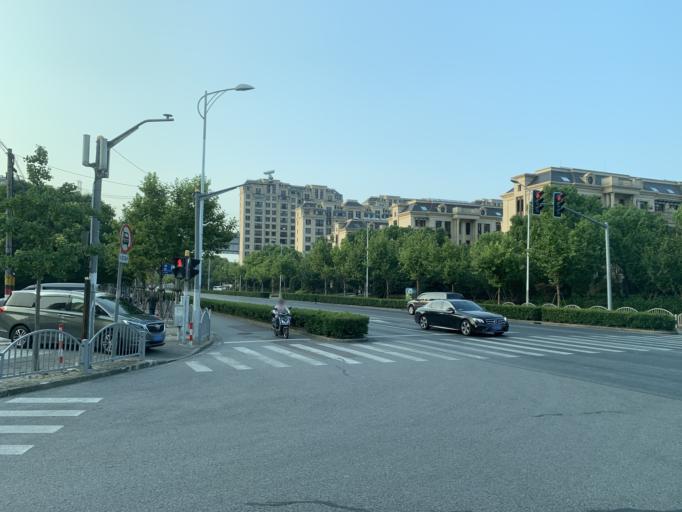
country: CN
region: Shanghai Shi
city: Huamu
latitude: 31.1871
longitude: 121.5423
